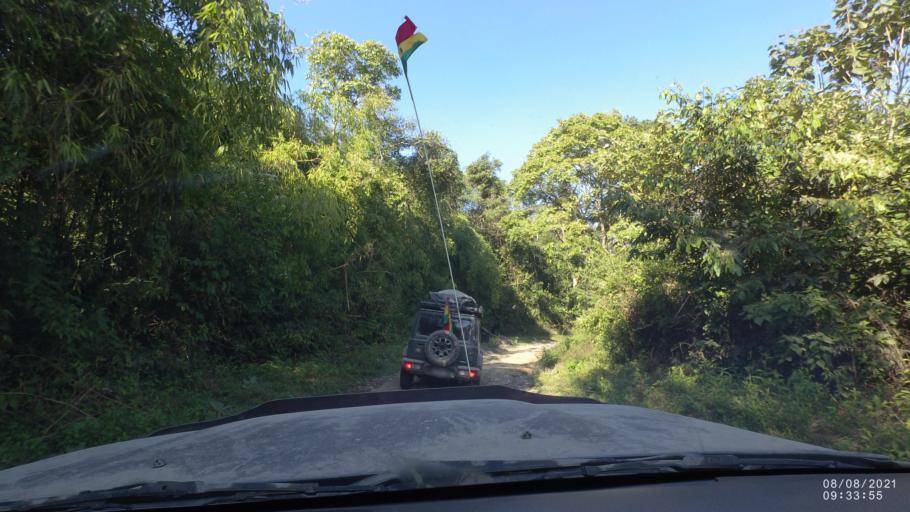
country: BO
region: La Paz
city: Quime
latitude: -16.5899
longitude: -66.7025
